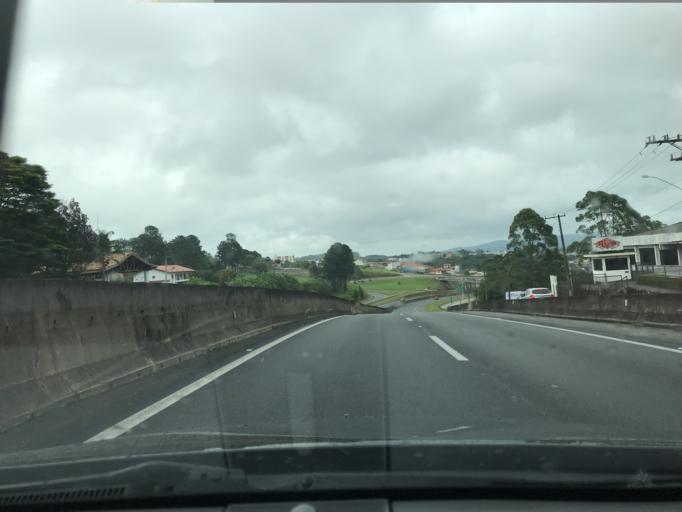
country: BR
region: Sao Paulo
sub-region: Vargem Grande Paulista
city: Vargem Grande Paulista
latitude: -23.6134
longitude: -46.9964
